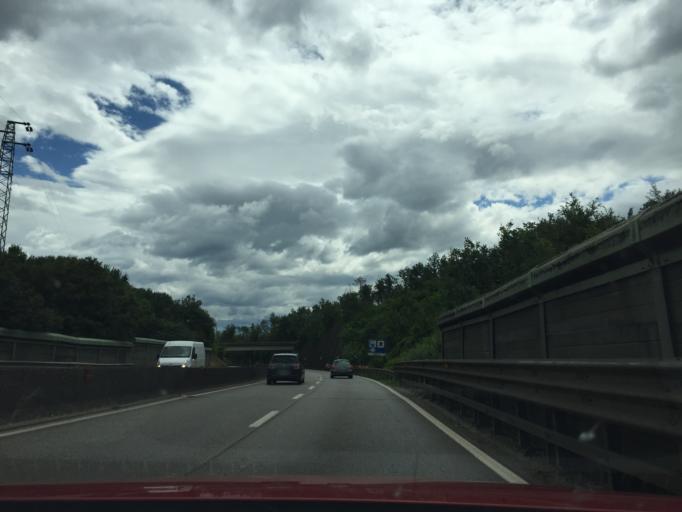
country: IT
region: Tuscany
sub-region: Province of Florence
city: Montelupo Fiorentino
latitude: 43.7172
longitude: 11.0341
